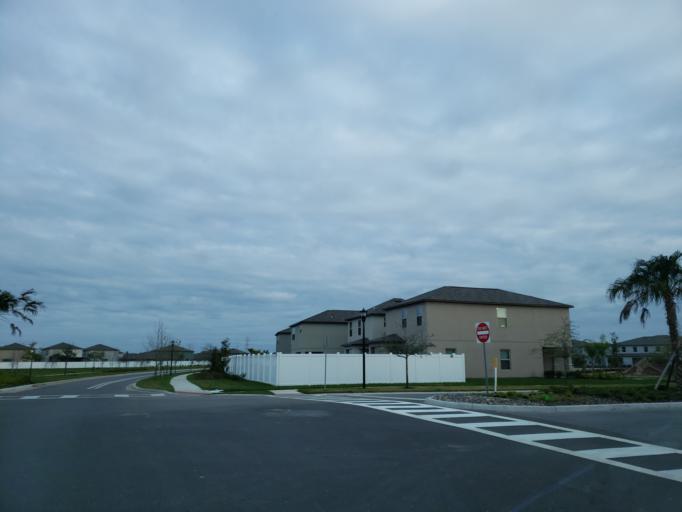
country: US
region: Florida
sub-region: Hillsborough County
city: Palm River-Clair Mel
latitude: 27.9117
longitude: -82.3750
